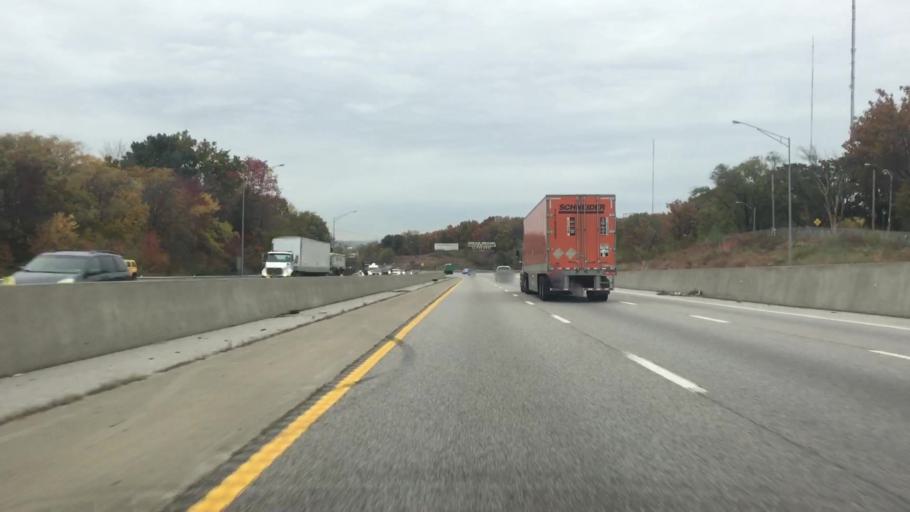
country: US
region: Missouri
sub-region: Jackson County
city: Sugar Creek
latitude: 39.0685
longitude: -94.4879
